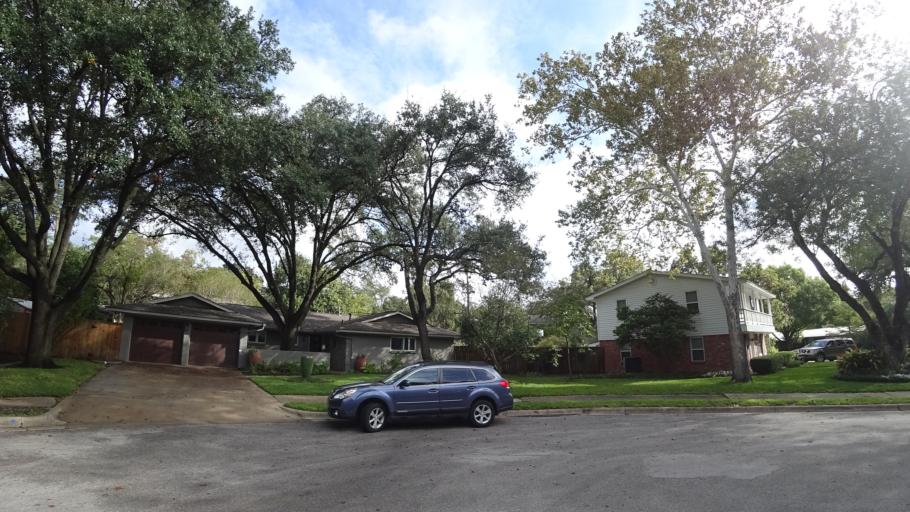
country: US
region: Texas
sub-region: Travis County
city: West Lake Hills
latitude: 30.3456
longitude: -97.7470
